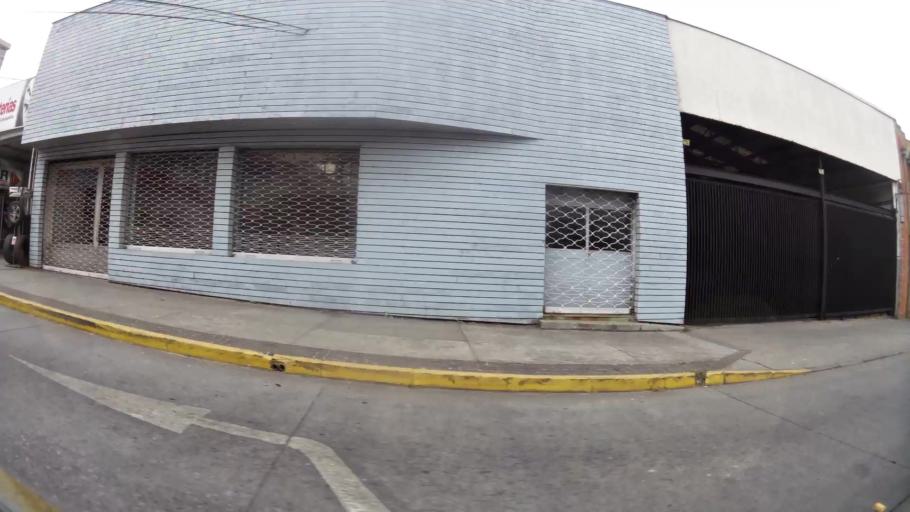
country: CL
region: Biobio
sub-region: Provincia de Concepcion
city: Concepcion
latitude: -36.8317
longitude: -73.0567
